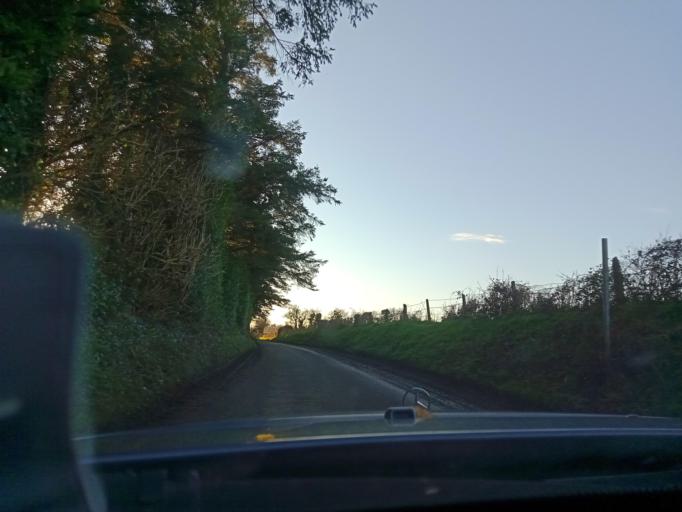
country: IE
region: Leinster
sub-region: Loch Garman
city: New Ross
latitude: 52.3883
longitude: -6.9859
